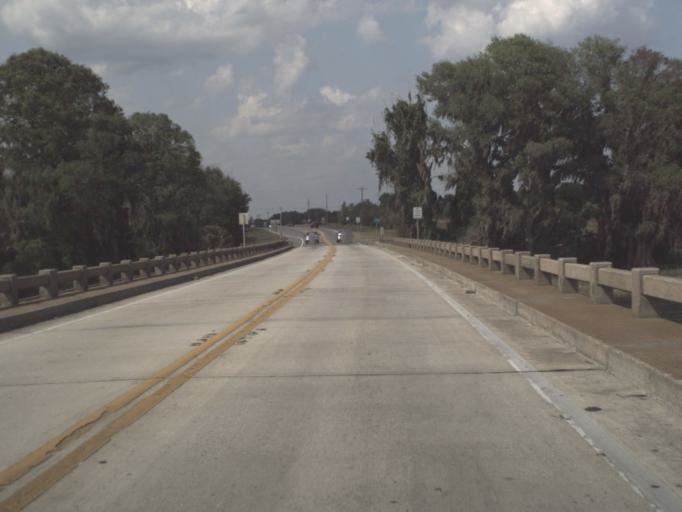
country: US
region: Florida
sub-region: Lake County
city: Howie In The Hills
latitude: 28.7422
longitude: -81.7660
